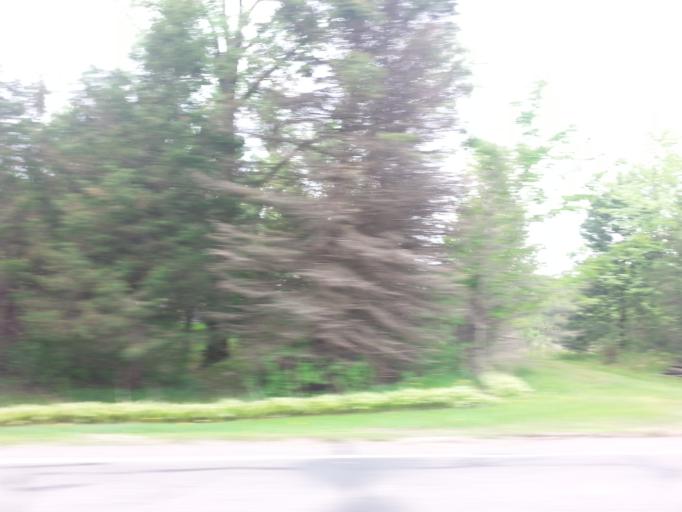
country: US
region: Wisconsin
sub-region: Saint Croix County
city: Hudson
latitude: 44.9802
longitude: -92.7819
